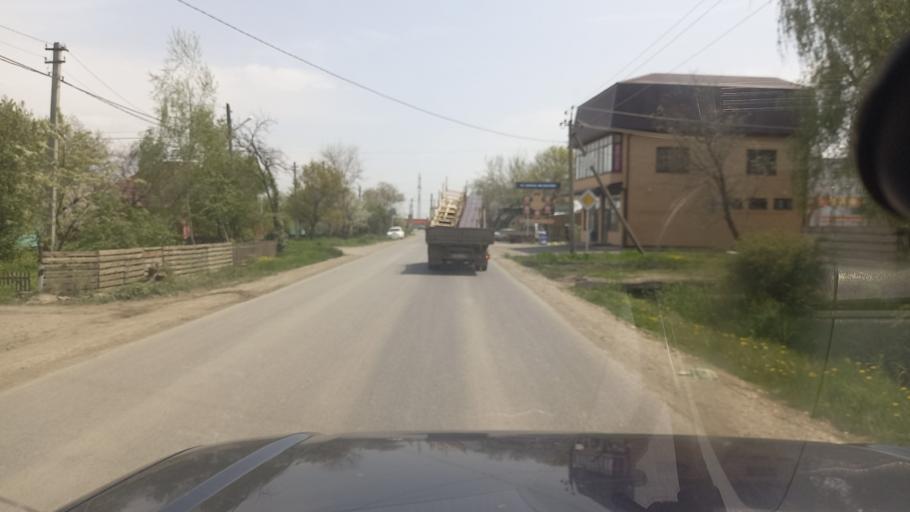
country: RU
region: Adygeya
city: Yablonovskiy
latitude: 44.9867
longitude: 38.9615
